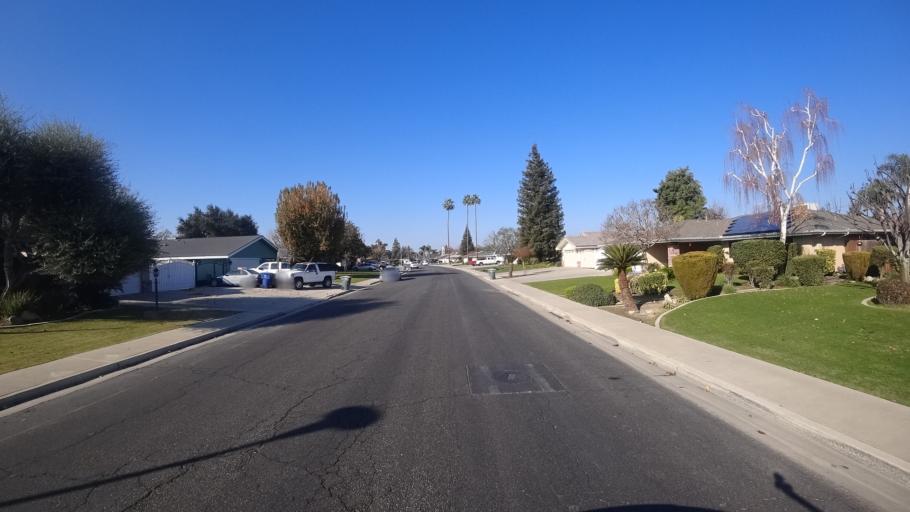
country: US
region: California
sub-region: Kern County
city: Greenacres
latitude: 35.3216
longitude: -119.1031
